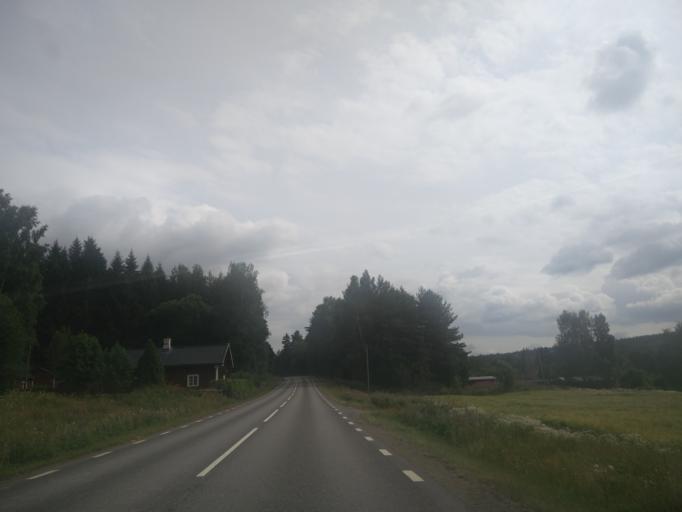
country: SE
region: Vaermland
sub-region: Arvika Kommun
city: Arvika
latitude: 59.7357
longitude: 12.5606
